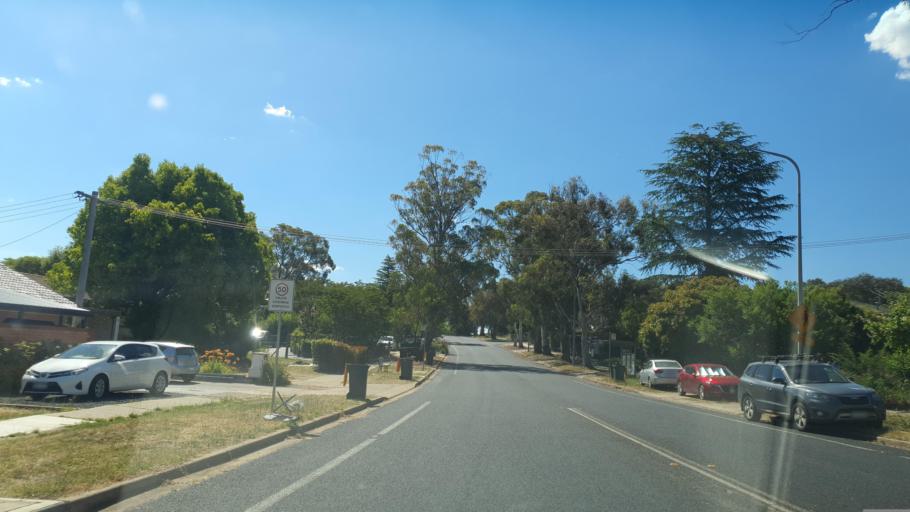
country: AU
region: Australian Capital Territory
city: Belconnen
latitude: -35.2135
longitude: 149.0457
